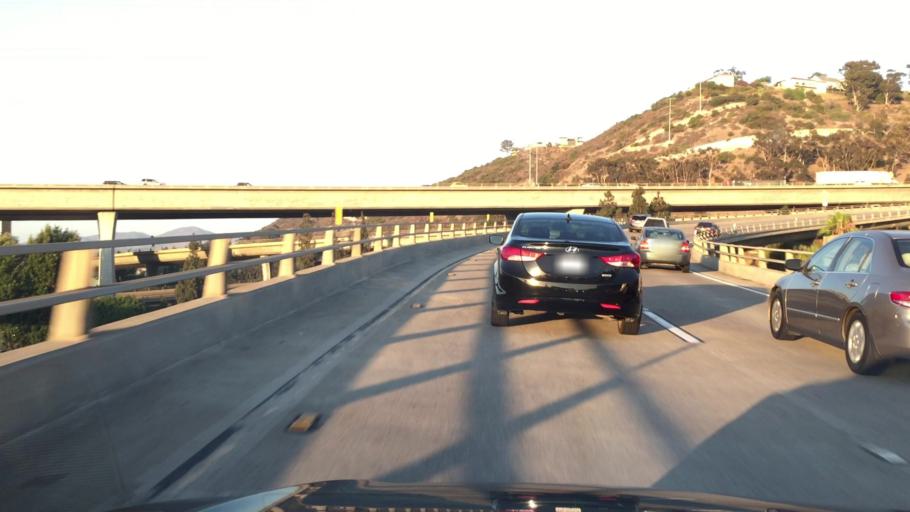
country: US
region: California
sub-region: San Diego County
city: San Diego
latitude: 32.7705
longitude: -117.1332
